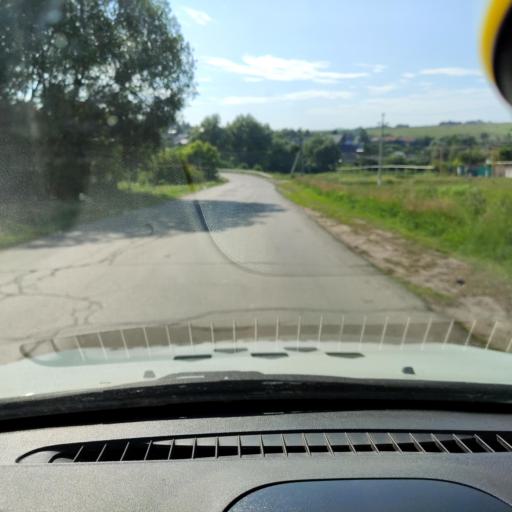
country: RU
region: Samara
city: Tol'yatti
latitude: 53.3559
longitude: 49.3080
